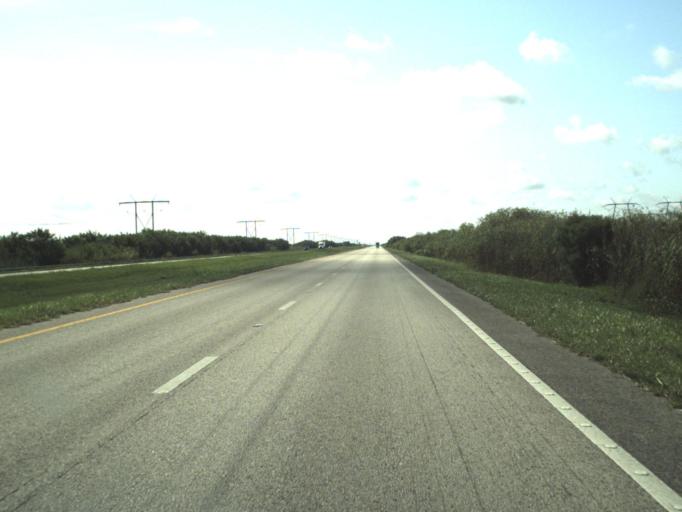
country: US
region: Florida
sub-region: Broward County
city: Weston
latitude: 26.2793
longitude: -80.4952
